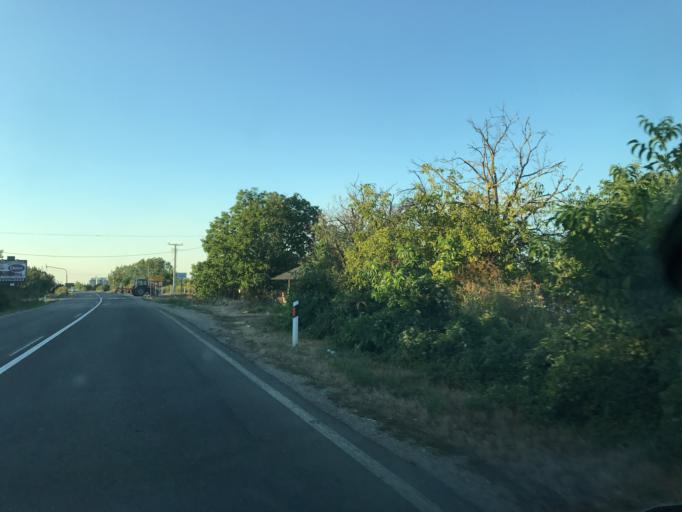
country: RS
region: Central Serbia
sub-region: Branicevski Okrug
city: Pozarevac
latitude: 44.6203
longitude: 21.1463
